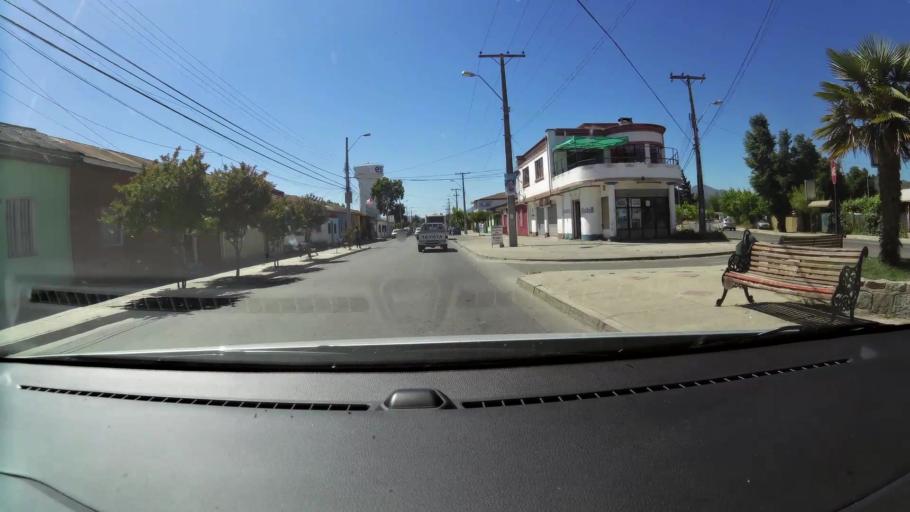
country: CL
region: Valparaiso
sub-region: Provincia de Marga Marga
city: Quilpue
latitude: -33.3246
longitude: -71.4021
